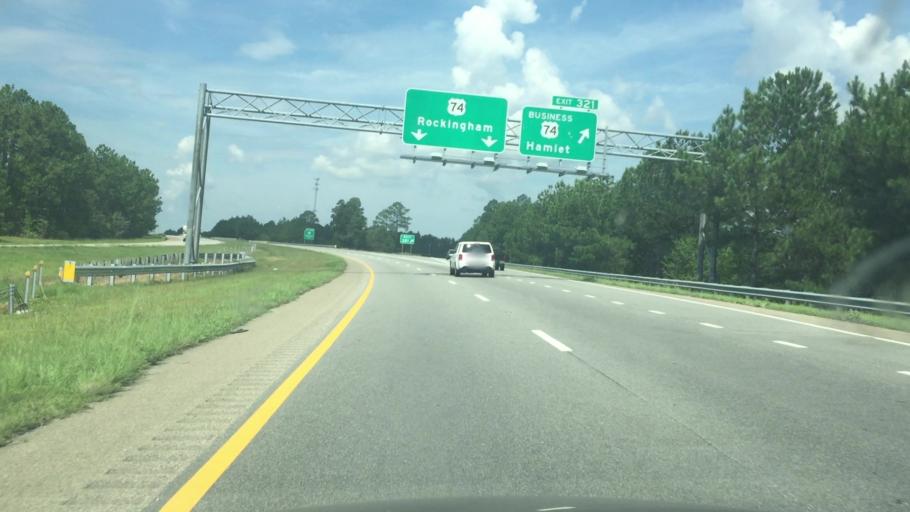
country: US
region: North Carolina
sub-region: Richmond County
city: Hamlet
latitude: 34.8688
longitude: -79.6456
